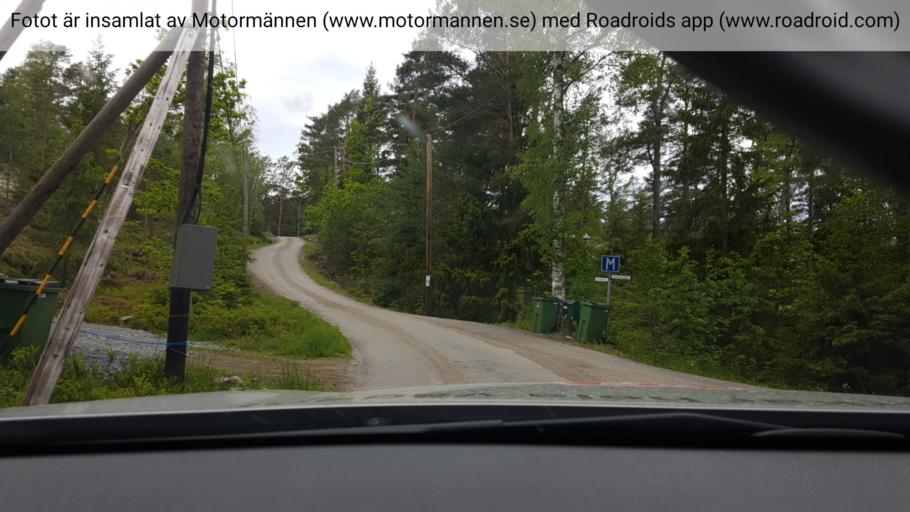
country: SE
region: Stockholm
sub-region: Haninge Kommun
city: Jordbro
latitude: 59.0184
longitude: 18.1113
